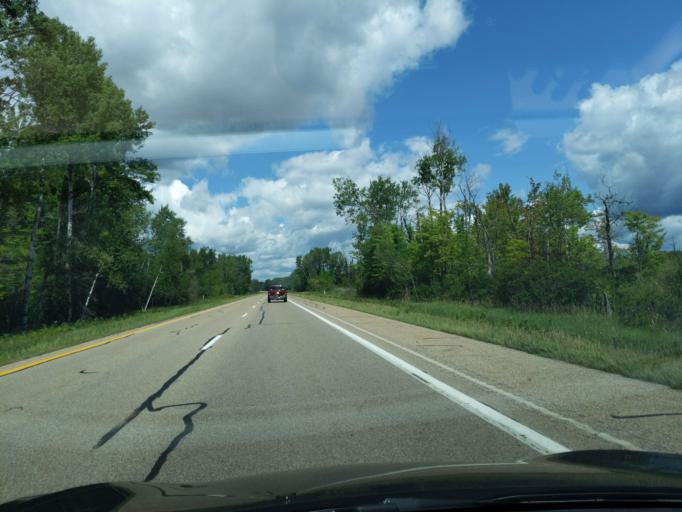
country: US
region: Michigan
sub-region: Roscommon County
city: Houghton Lake
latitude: 44.2883
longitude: -84.7998
